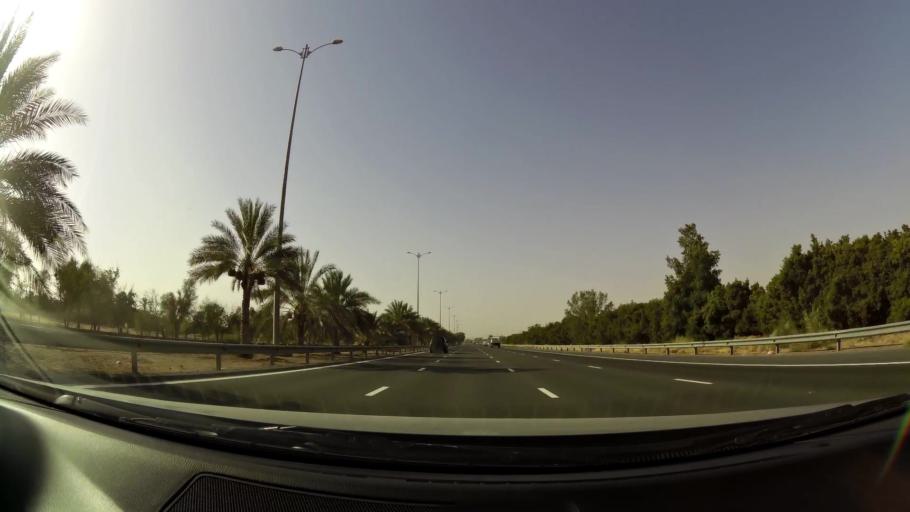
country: OM
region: Al Buraimi
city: Al Buraymi
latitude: 24.6061
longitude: 55.7309
